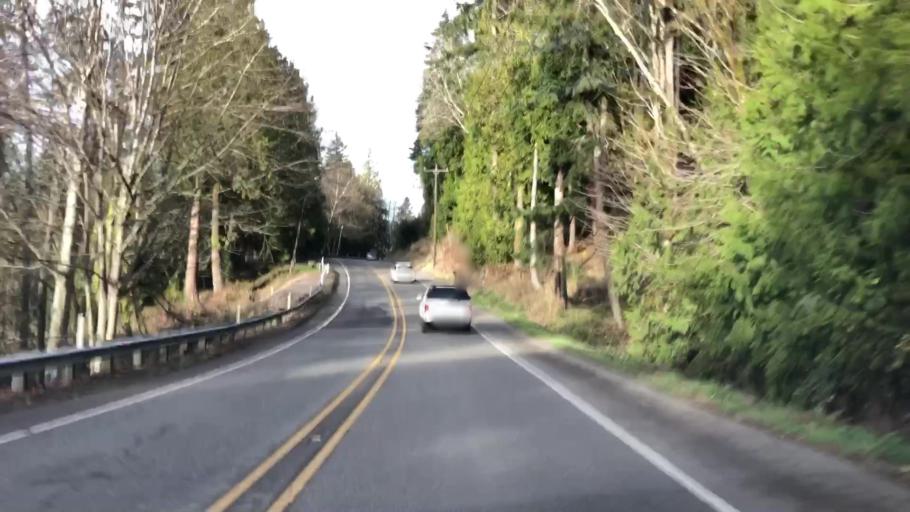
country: US
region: Washington
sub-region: Kitsap County
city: Suquamish
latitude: 47.7561
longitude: -122.5491
